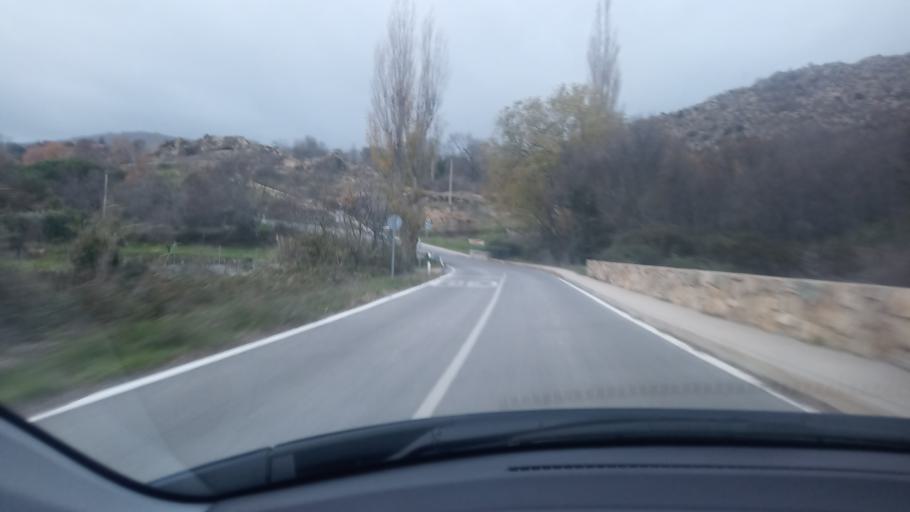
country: ES
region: Madrid
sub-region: Provincia de Madrid
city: Zarzalejo
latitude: 40.5463
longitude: -4.1715
